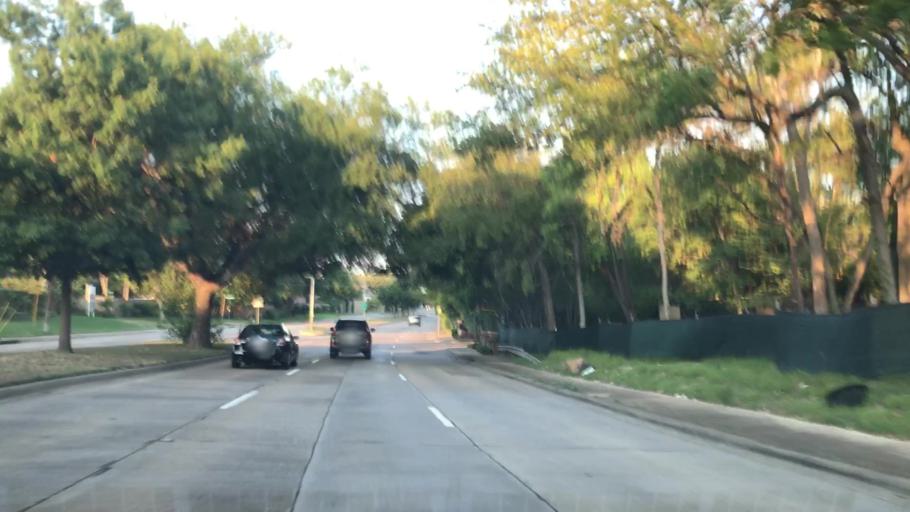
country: US
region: Texas
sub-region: Dallas County
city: University Park
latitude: 32.9095
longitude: -96.7923
